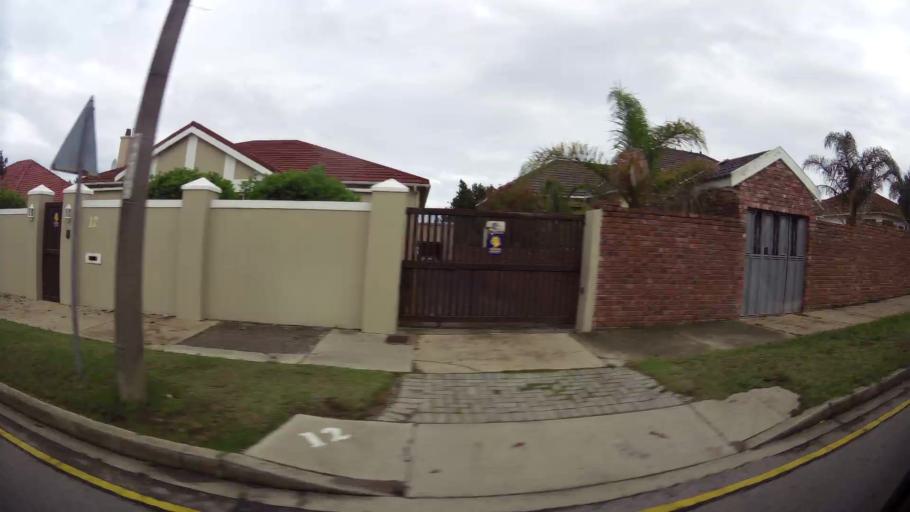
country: ZA
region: Eastern Cape
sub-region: Nelson Mandela Bay Metropolitan Municipality
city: Port Elizabeth
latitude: -33.9567
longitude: 25.5961
